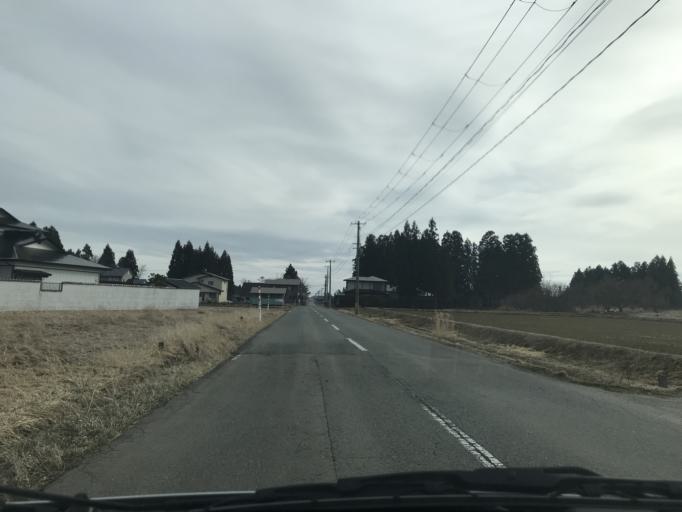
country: JP
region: Iwate
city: Hanamaki
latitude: 39.3961
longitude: 141.0748
